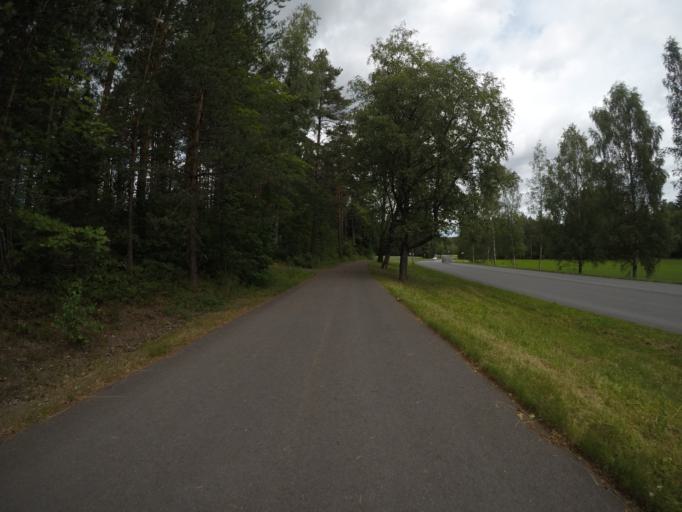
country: FI
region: Haeme
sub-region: Haemeenlinna
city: Haemeenlinna
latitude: 60.9705
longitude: 24.4369
